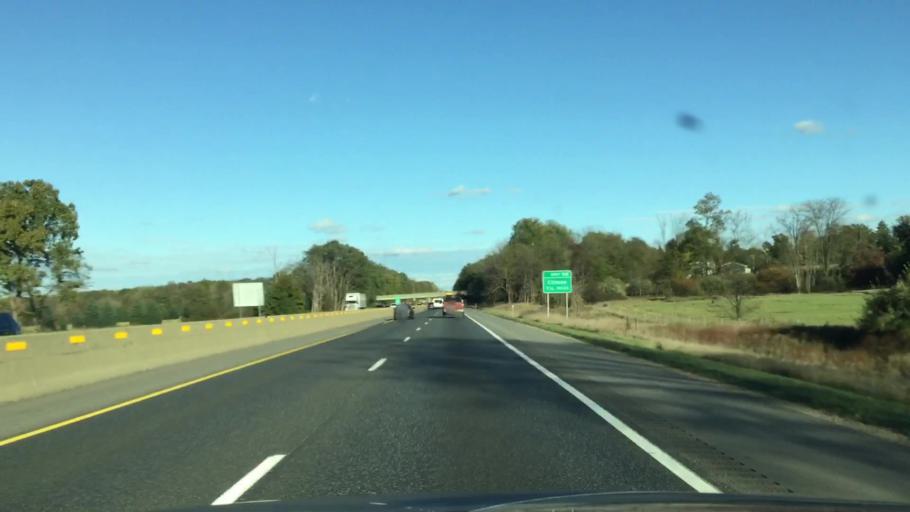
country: US
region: Michigan
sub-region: Kalamazoo County
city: Galesburg
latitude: 42.2776
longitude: -85.4059
